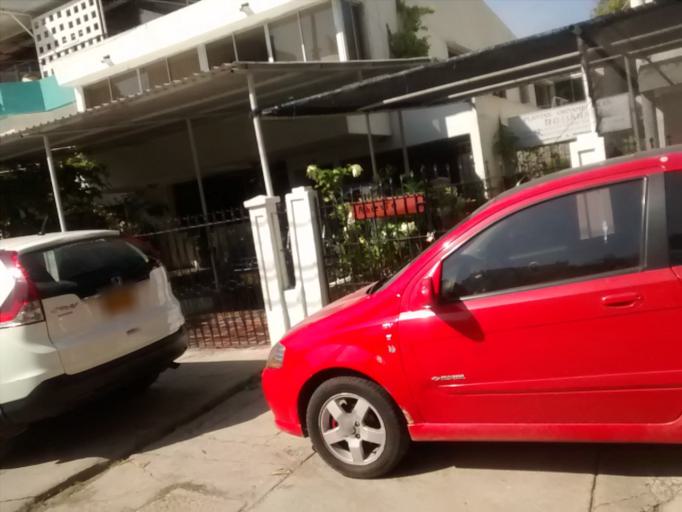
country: CO
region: Bolivar
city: Cartagena
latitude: 10.3935
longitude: -75.5498
